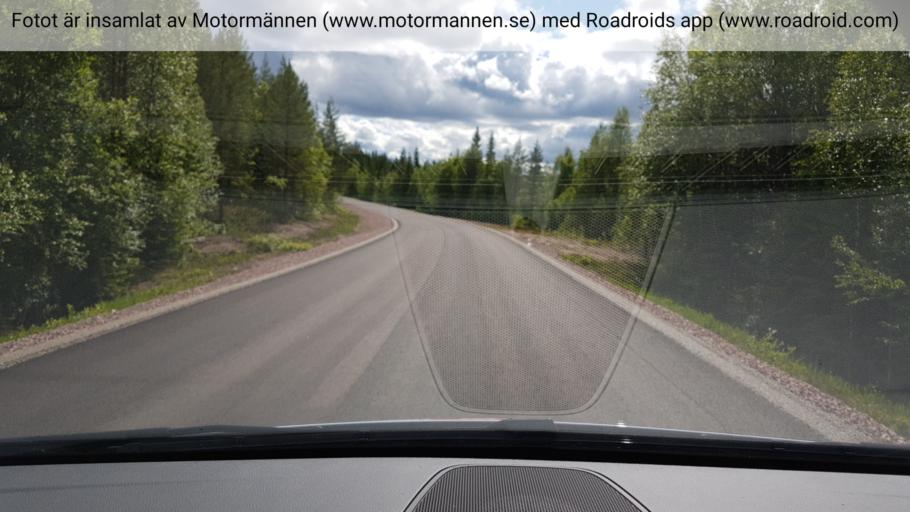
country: SE
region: Jaemtland
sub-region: Harjedalens Kommun
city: Sveg
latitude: 61.6763
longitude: 14.1692
